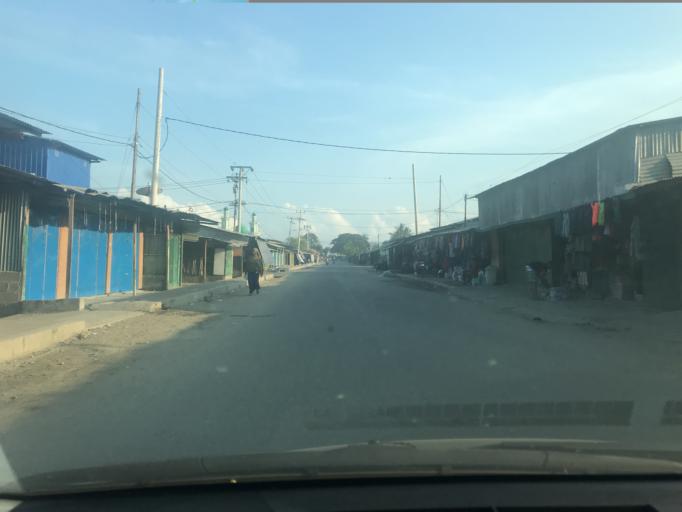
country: TL
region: Dili
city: Dili
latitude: -8.5523
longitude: 125.5607
